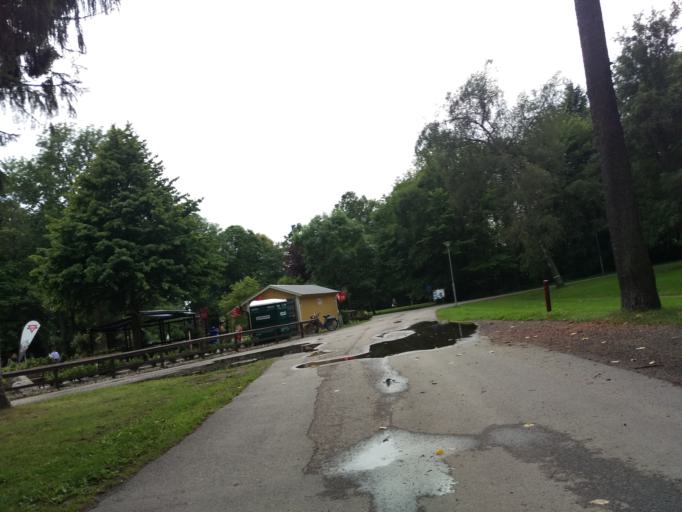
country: SE
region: OEstergoetland
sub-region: Norrkopings Kommun
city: Norrkoping
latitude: 58.5906
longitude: 16.1647
